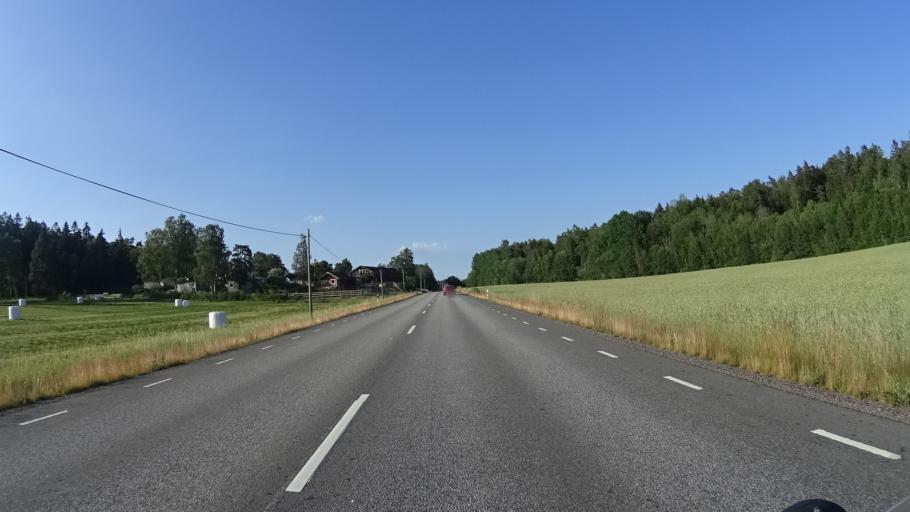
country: SE
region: Stockholm
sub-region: Sodertalje Kommun
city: Pershagen
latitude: 59.0926
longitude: 17.6173
